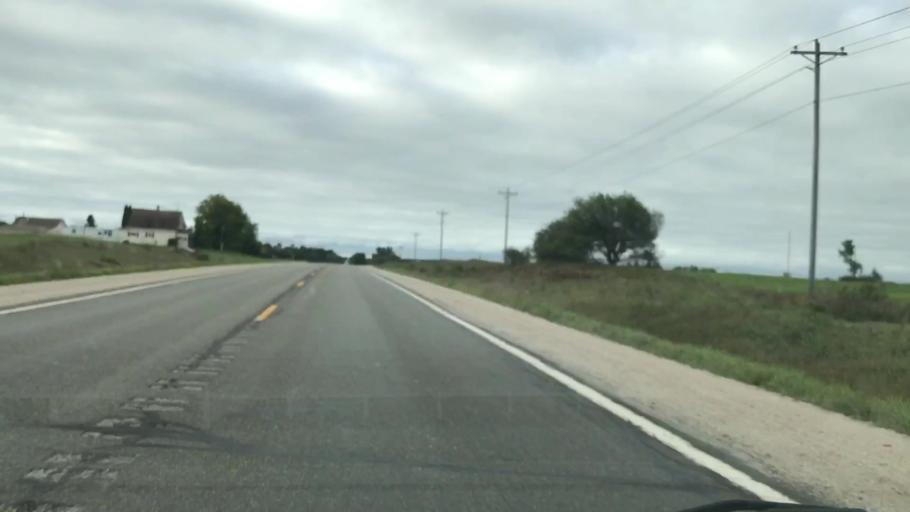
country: US
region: Michigan
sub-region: Luce County
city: Newberry
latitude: 46.1654
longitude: -85.5713
